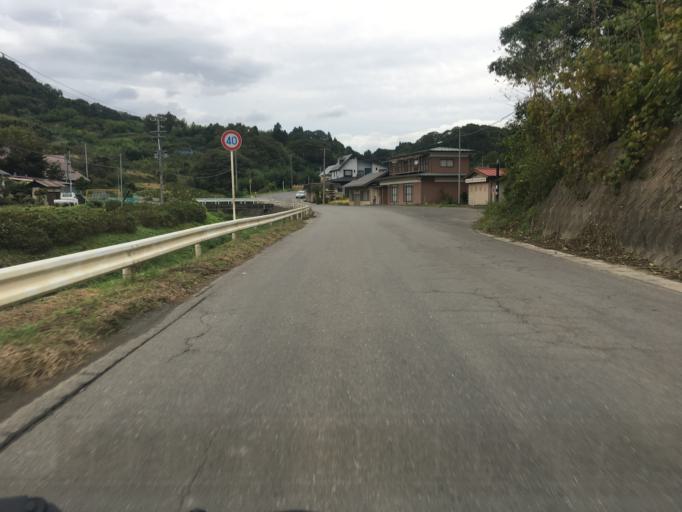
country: JP
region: Fukushima
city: Yanagawamachi-saiwaicho
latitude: 37.8820
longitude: 140.6684
